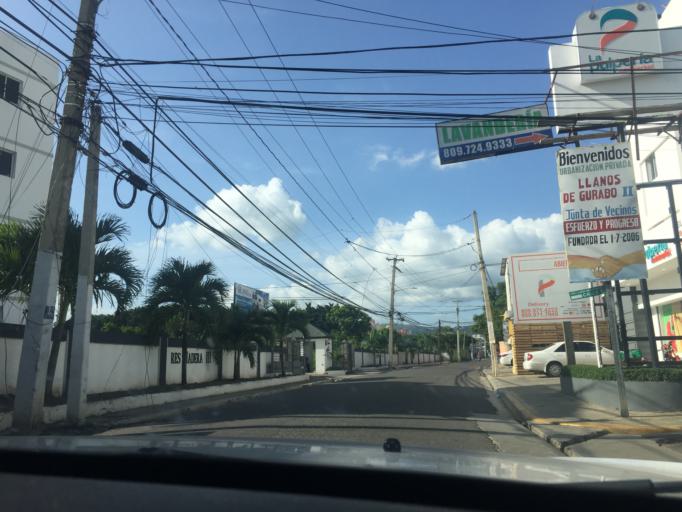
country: DO
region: Santiago
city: Santiago de los Caballeros
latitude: 19.4739
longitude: -70.6569
